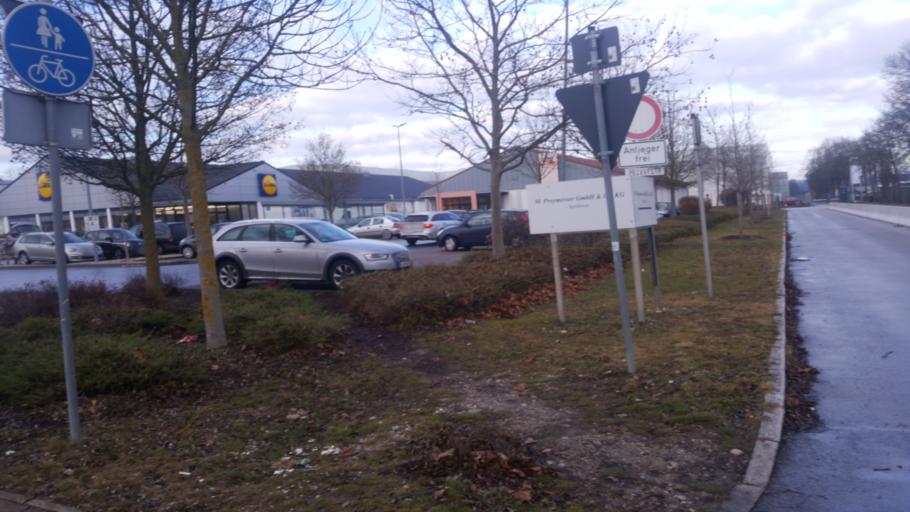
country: DE
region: Bavaria
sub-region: Upper Bavaria
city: Neufahrn bei Freising
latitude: 48.3112
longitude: 11.6468
